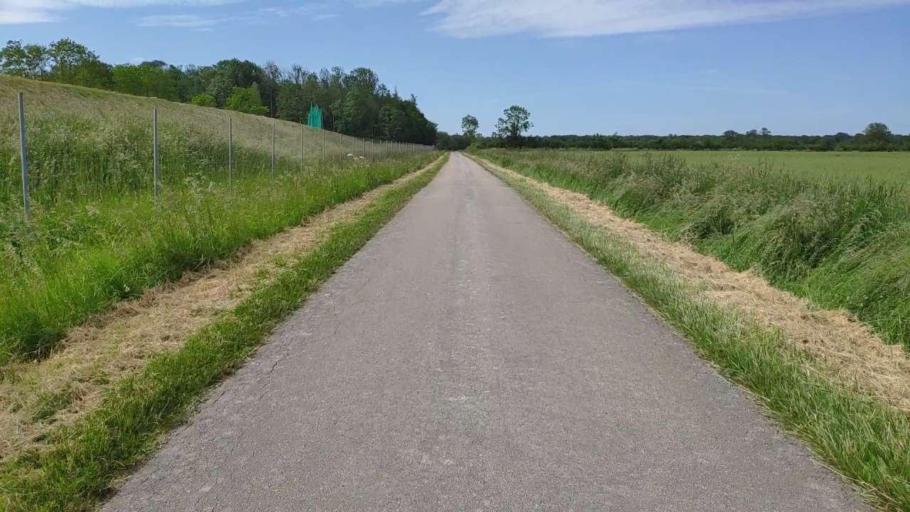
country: FR
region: Franche-Comte
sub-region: Departement du Jura
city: Bletterans
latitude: 46.6855
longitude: 5.4281
